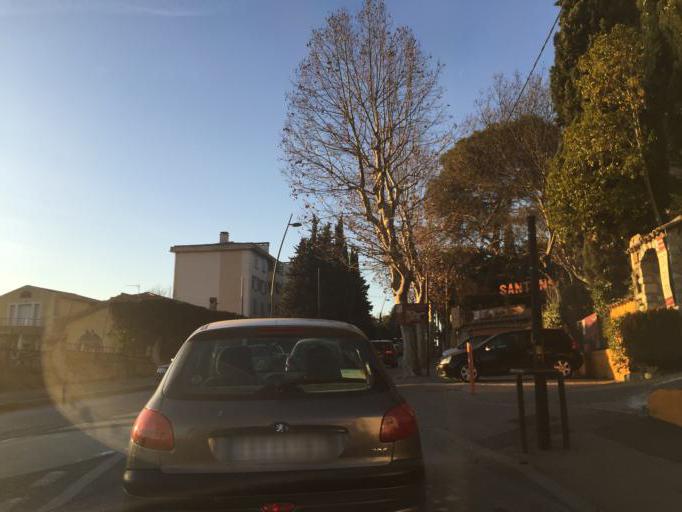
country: FR
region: Provence-Alpes-Cote d'Azur
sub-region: Departement des Bouches-du-Rhone
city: Aix-en-Provence
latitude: 43.5193
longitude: 5.4621
